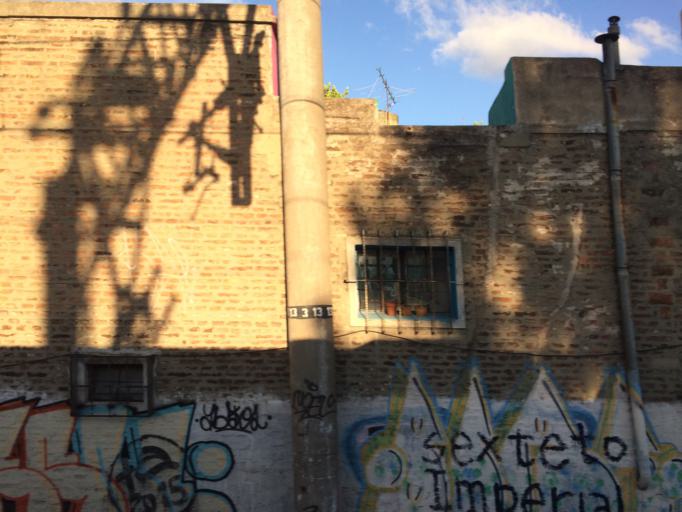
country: AR
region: Buenos Aires
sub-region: Partido de Lomas de Zamora
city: Lomas de Zamora
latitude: -34.7461
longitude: -58.3955
